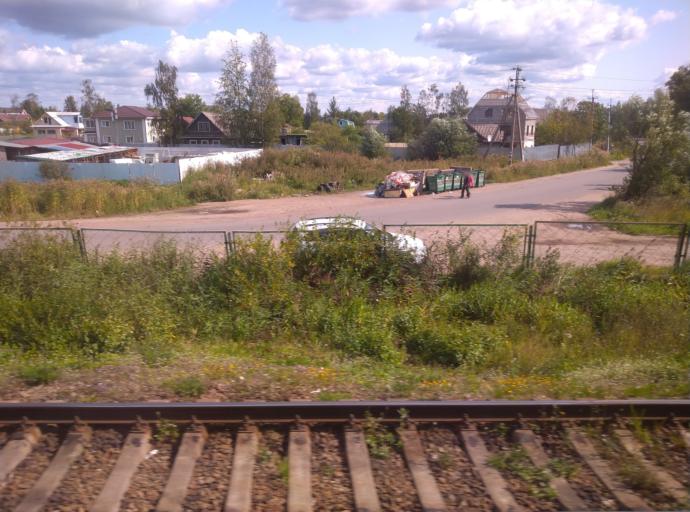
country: RU
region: Leningrad
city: Ul'yanovka
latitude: 59.6334
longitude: 30.7604
